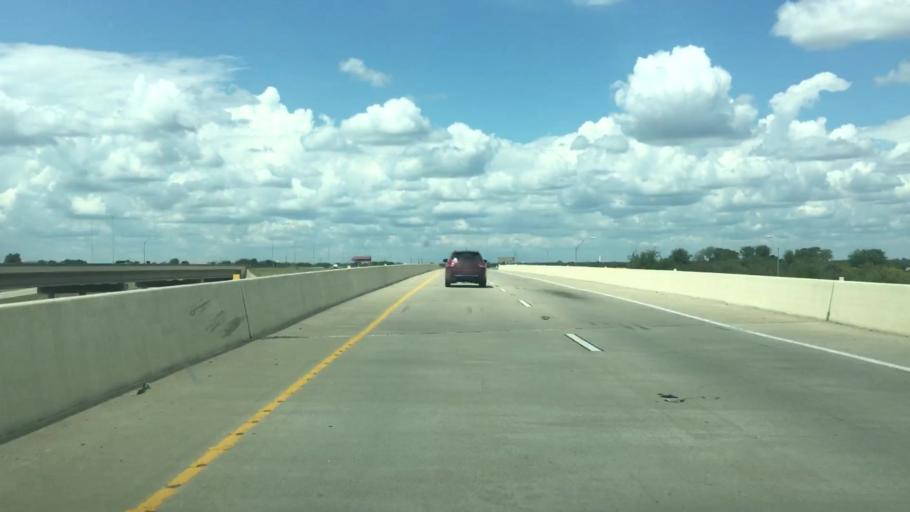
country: US
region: Texas
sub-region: Williamson County
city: Georgetown
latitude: 30.6211
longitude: -97.6145
